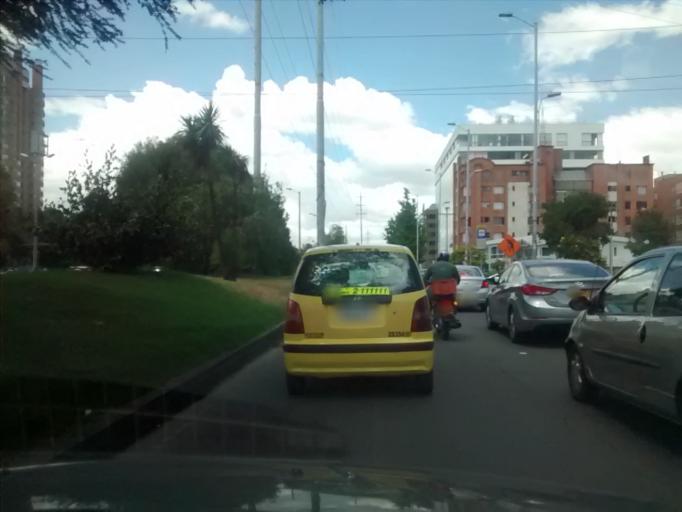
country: CO
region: Bogota D.C.
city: Barrio San Luis
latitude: 4.6967
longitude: -74.0552
